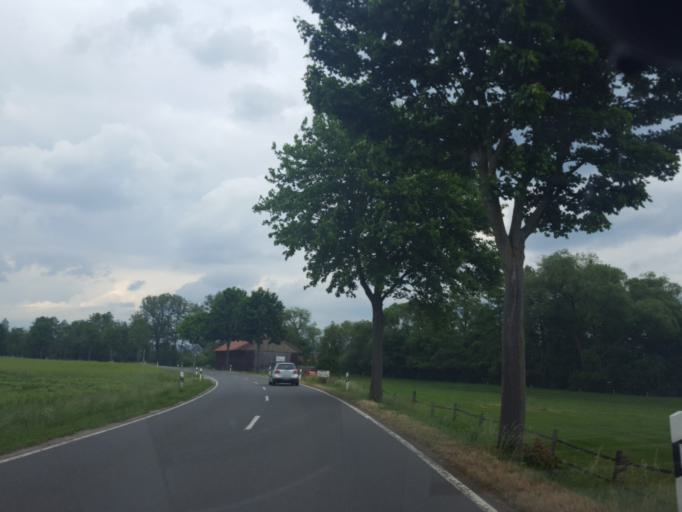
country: DE
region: Lower Saxony
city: Eisdorf am Harz
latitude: 51.7379
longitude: 10.1697
